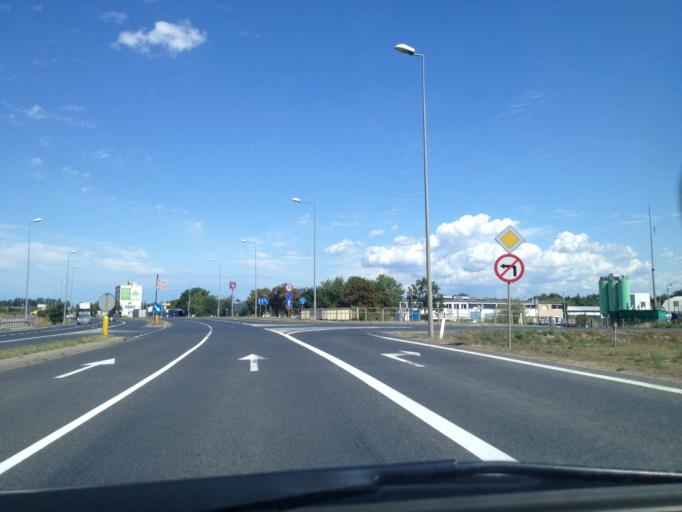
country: PL
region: Lower Silesian Voivodeship
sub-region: Legnica
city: Legnica
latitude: 51.1672
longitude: 16.1730
